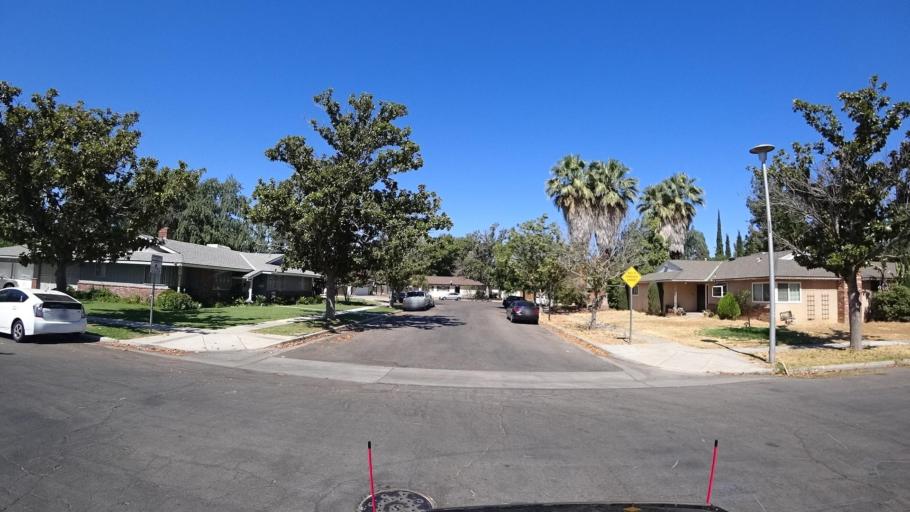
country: US
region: California
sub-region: Fresno County
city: Fresno
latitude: 36.7382
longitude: -119.7757
